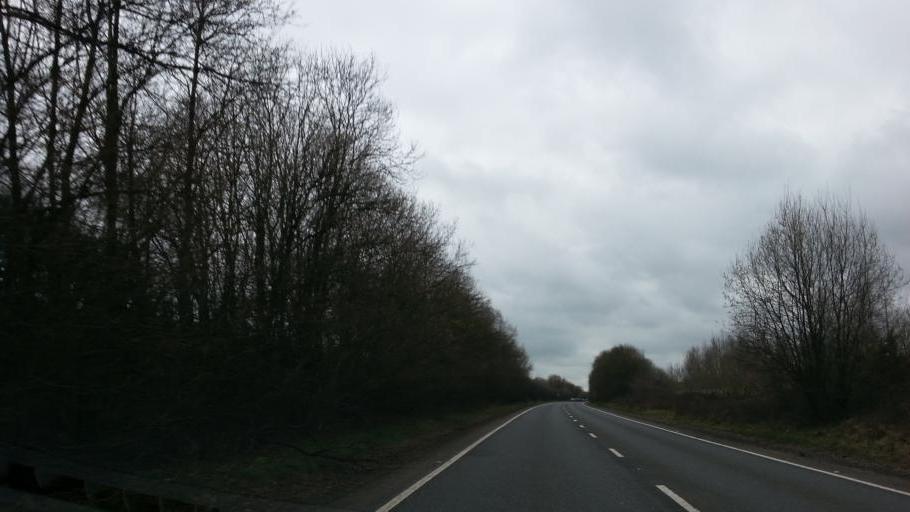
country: GB
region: England
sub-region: Devon
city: South Molton
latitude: 51.0300
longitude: -3.8333
